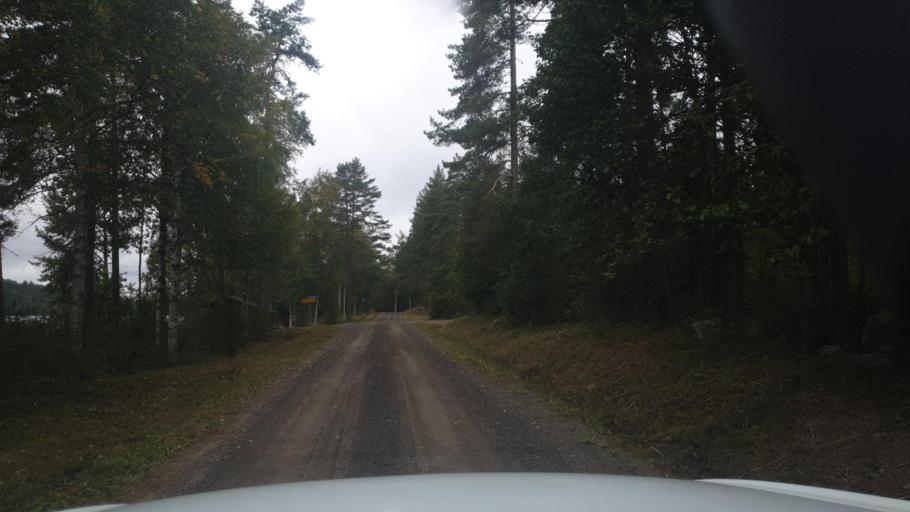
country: SE
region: Vaermland
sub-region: Arvika Kommun
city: Arvika
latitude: 59.8686
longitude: 12.8069
